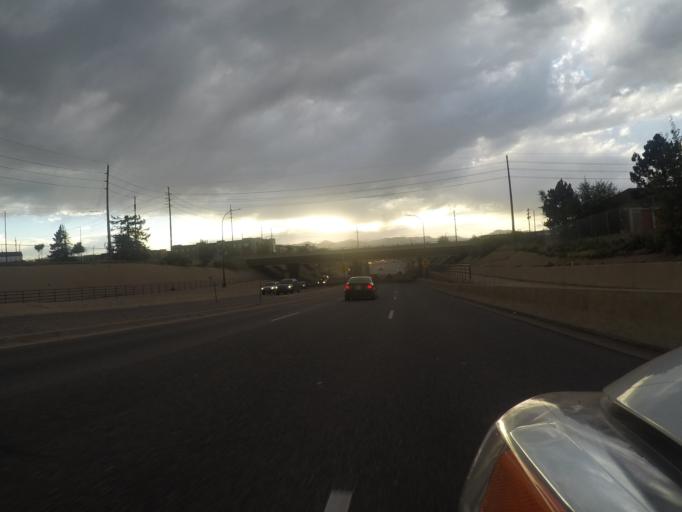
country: US
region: Colorado
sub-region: Arapahoe County
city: Littleton
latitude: 39.6242
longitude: -105.0092
